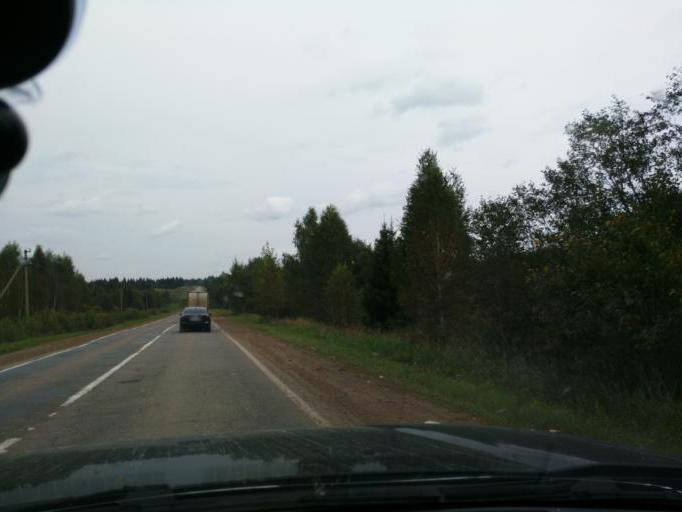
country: RU
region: Bashkortostan
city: Verkhniye Tatyshly
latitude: 56.4900
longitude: 55.8118
